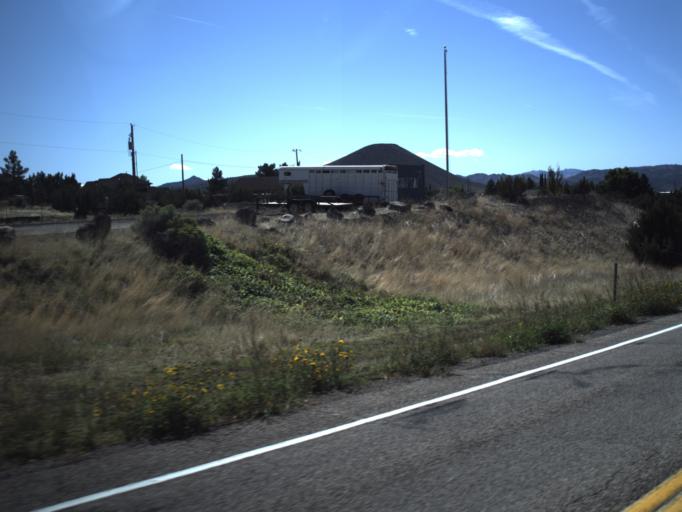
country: US
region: Utah
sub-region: Washington County
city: Ivins
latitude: 37.3487
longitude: -113.6899
